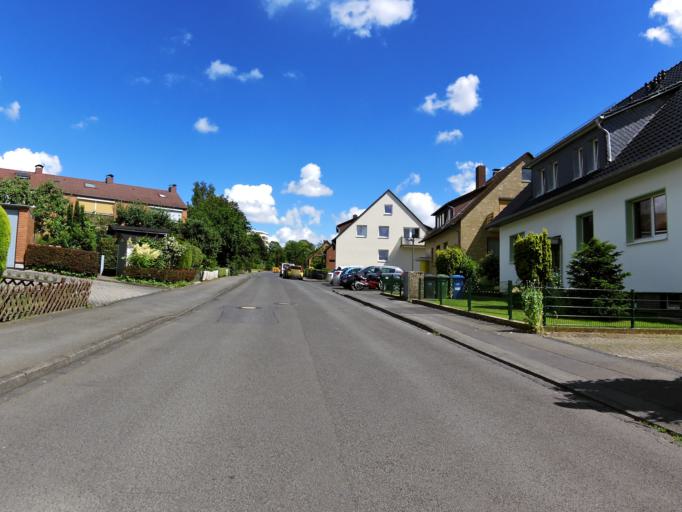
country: DE
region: Lower Saxony
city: Goettingen
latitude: 51.5073
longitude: 9.9611
